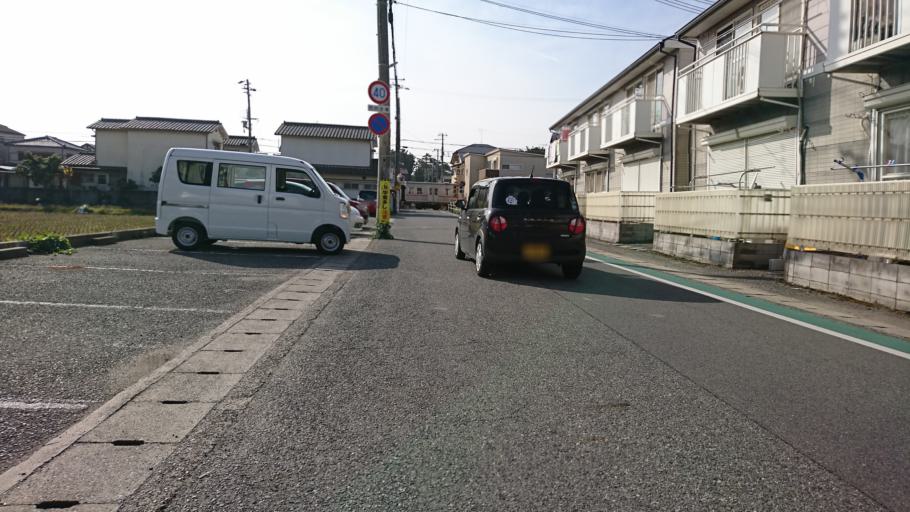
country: JP
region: Hyogo
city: Kakogawacho-honmachi
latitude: 34.7398
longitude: 134.8369
